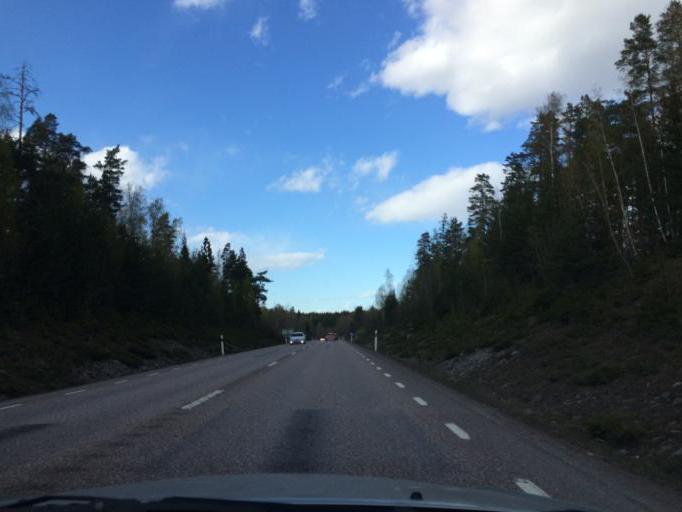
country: SE
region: Soedermanland
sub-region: Eskilstuna Kommun
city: Kvicksund
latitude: 59.5206
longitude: 16.3232
